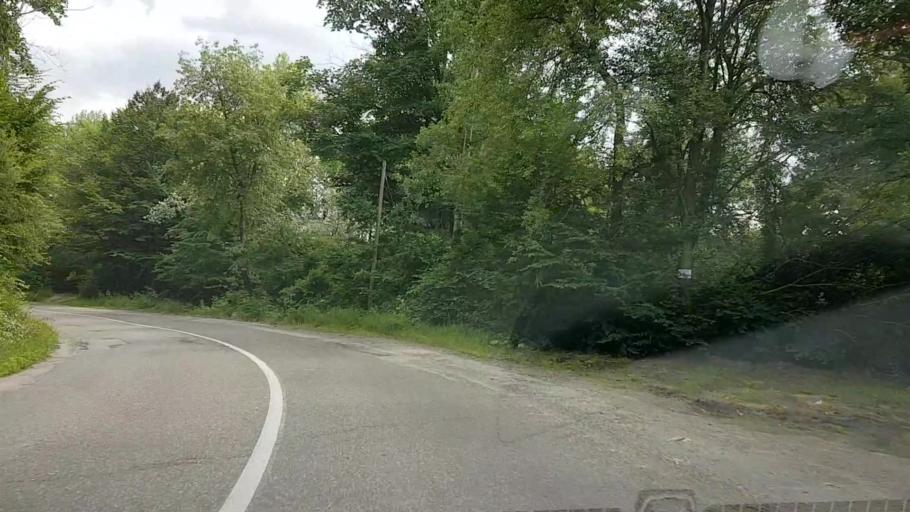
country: RO
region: Neamt
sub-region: Comuna Ceahlau
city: Ceahlau
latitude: 47.0536
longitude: 25.9743
